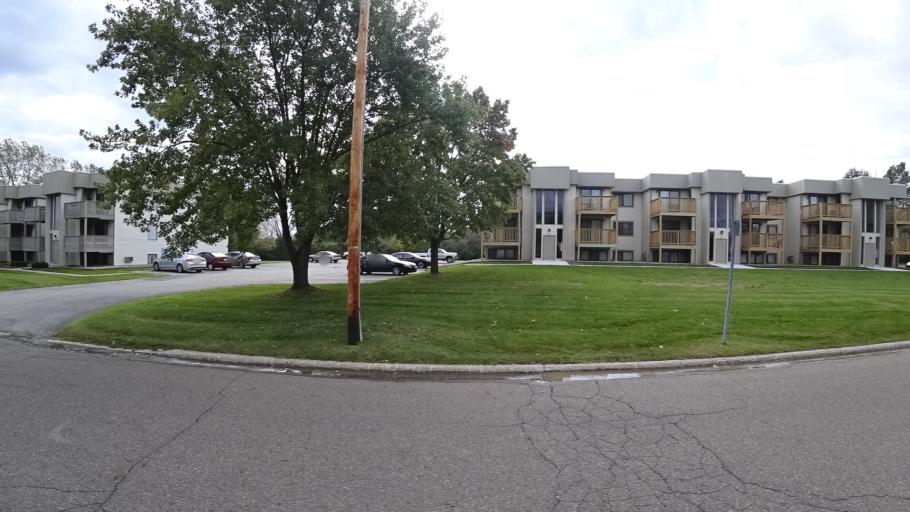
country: US
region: Indiana
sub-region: LaPorte County
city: Michigan City
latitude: 41.6688
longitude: -86.8969
